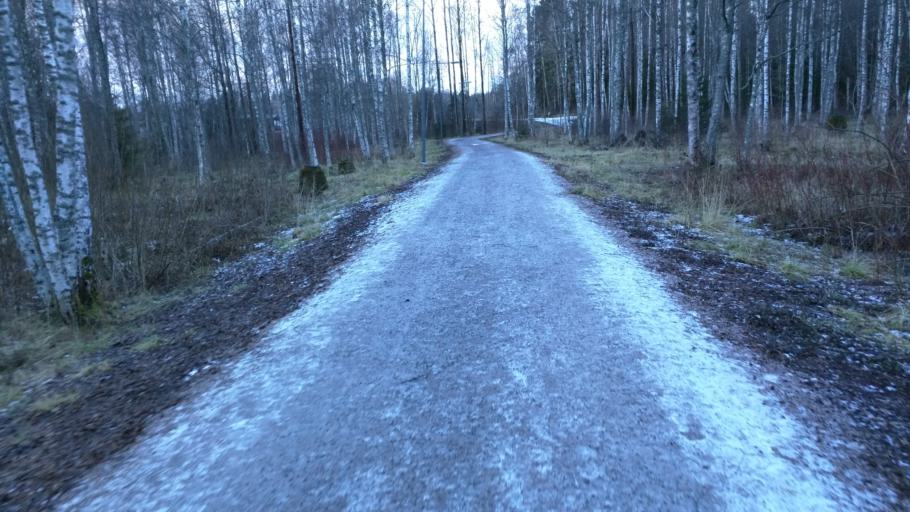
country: FI
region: Uusimaa
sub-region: Helsinki
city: Kauniainen
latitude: 60.2389
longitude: 24.7320
